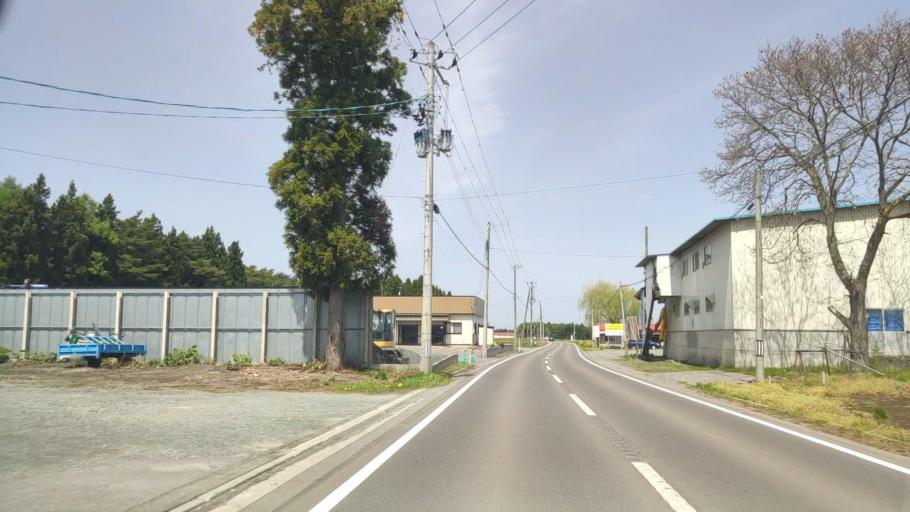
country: JP
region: Aomori
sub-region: Hachinohe Shi
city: Uchimaru
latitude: 40.5372
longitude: 141.4017
